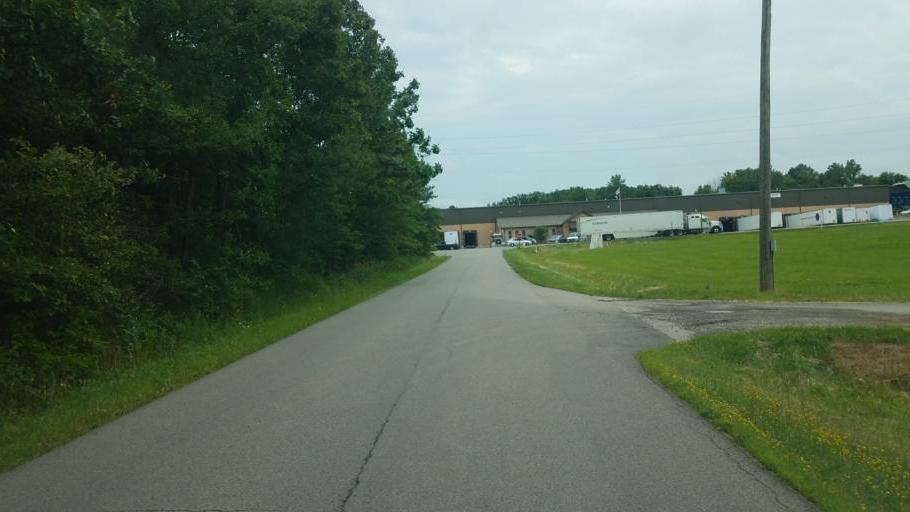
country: US
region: Ohio
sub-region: Richland County
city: Ontario
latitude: 40.7772
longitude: -82.5648
